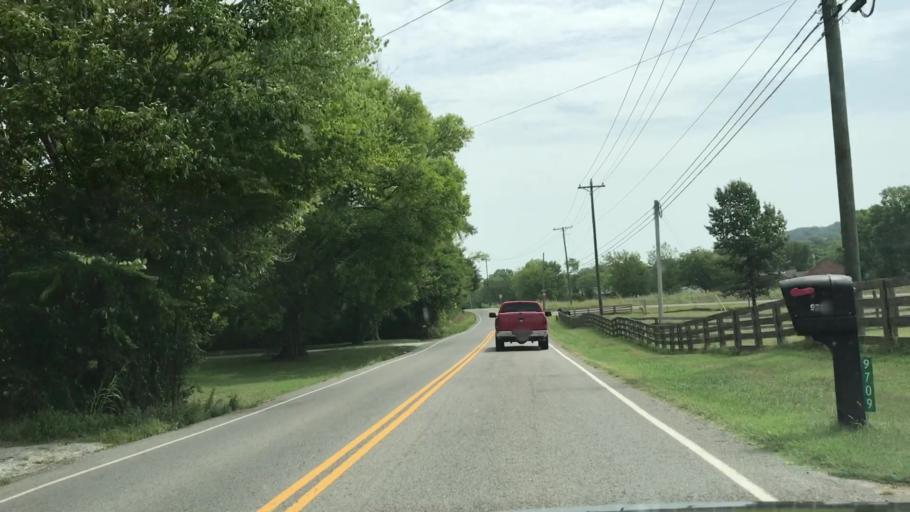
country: US
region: Tennessee
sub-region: Williamson County
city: Nolensville
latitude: 35.9379
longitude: -86.6884
